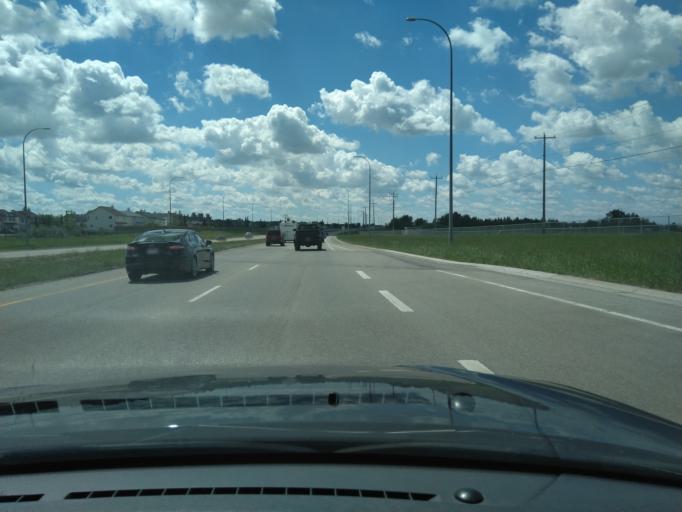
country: CA
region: Alberta
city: Calgary
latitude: 51.1218
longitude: -113.9702
